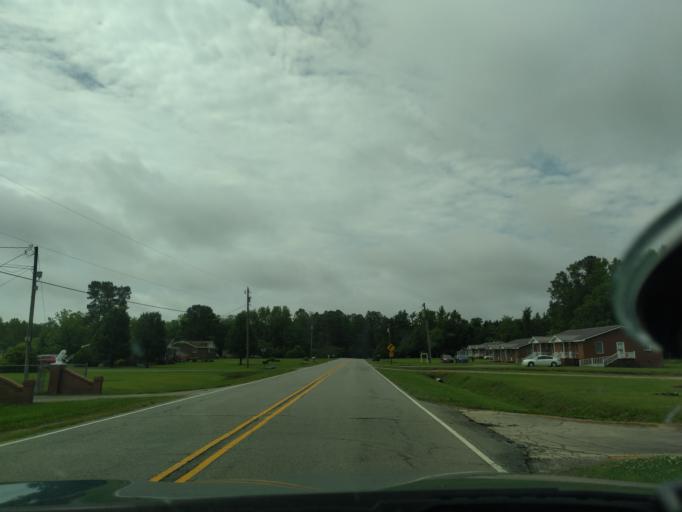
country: US
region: North Carolina
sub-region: Chowan County
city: Edenton
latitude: 35.9104
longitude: -76.6028
